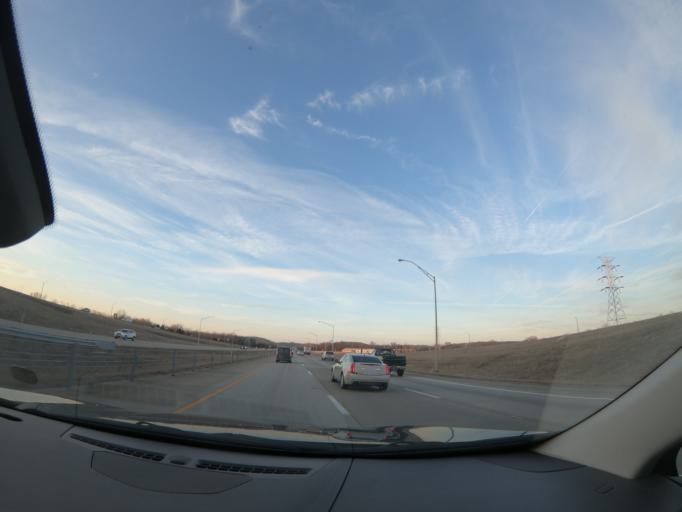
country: US
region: Kentucky
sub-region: Bullitt County
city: Shepherdsville
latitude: 37.9252
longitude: -85.6875
